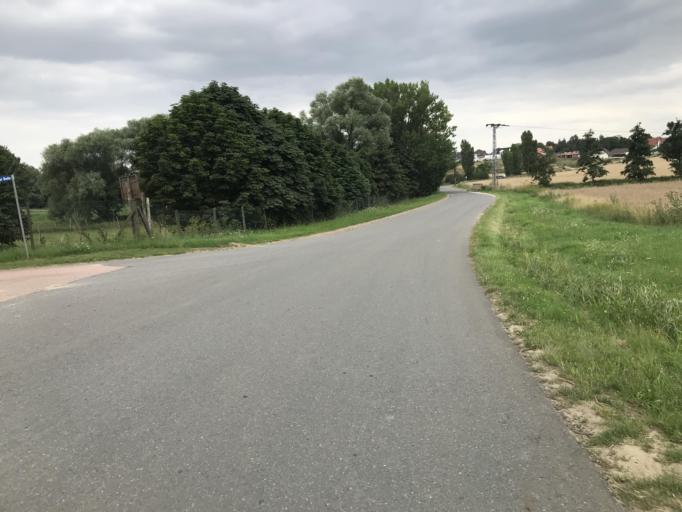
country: DE
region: Saxony-Anhalt
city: Quedlinburg
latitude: 51.8058
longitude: 11.1661
